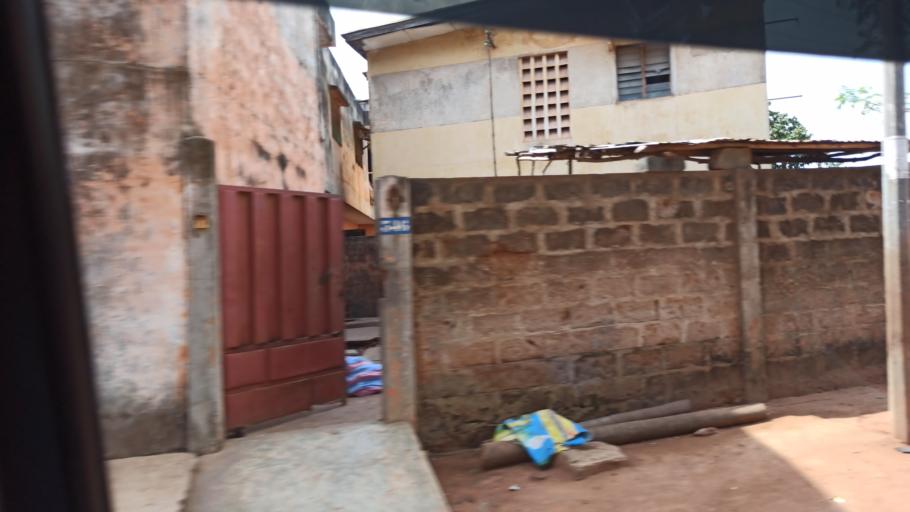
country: BJ
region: Queme
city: Porto-Novo
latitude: 6.4808
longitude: 2.6133
